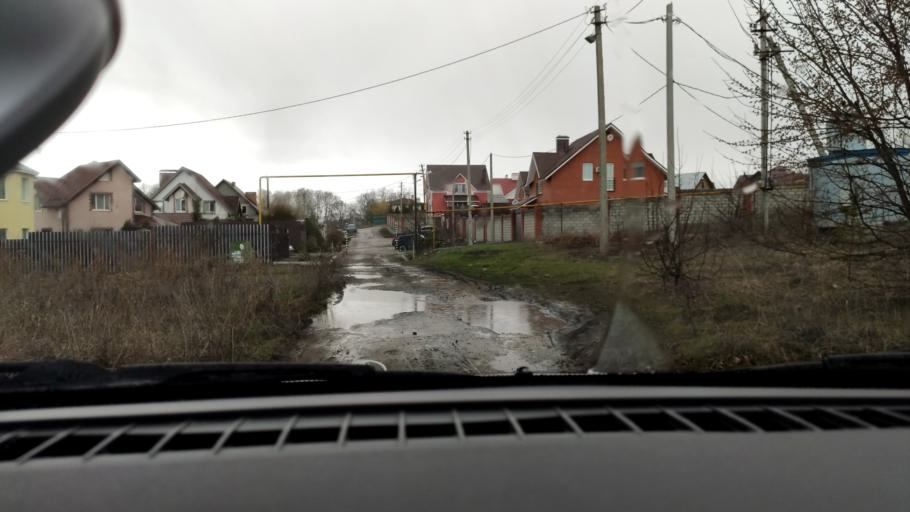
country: RU
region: Samara
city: Novosemeykino
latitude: 53.3300
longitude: 50.2888
